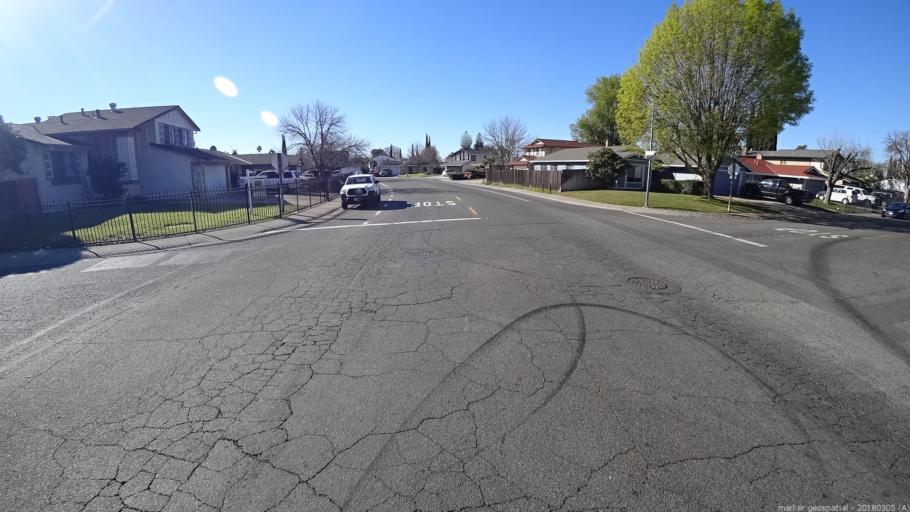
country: US
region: California
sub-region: Sacramento County
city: Florin
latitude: 38.4865
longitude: -121.4140
